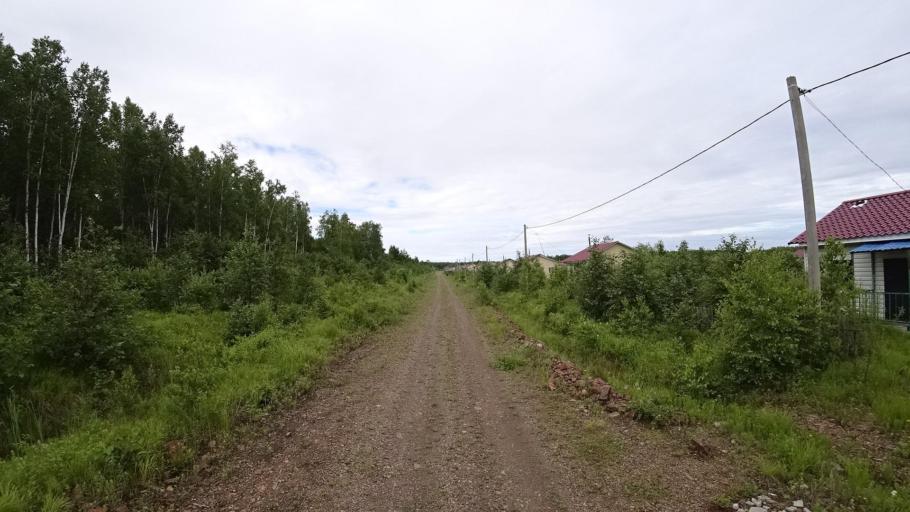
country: RU
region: Khabarovsk Krai
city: Amursk
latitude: 49.8979
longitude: 136.1656
